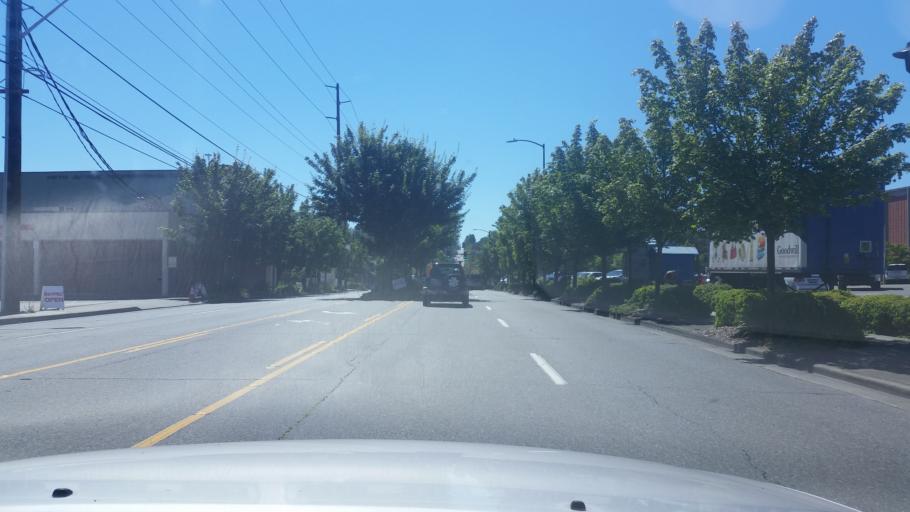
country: US
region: Washington
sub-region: King County
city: Shoreline
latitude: 47.7074
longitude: -122.3233
